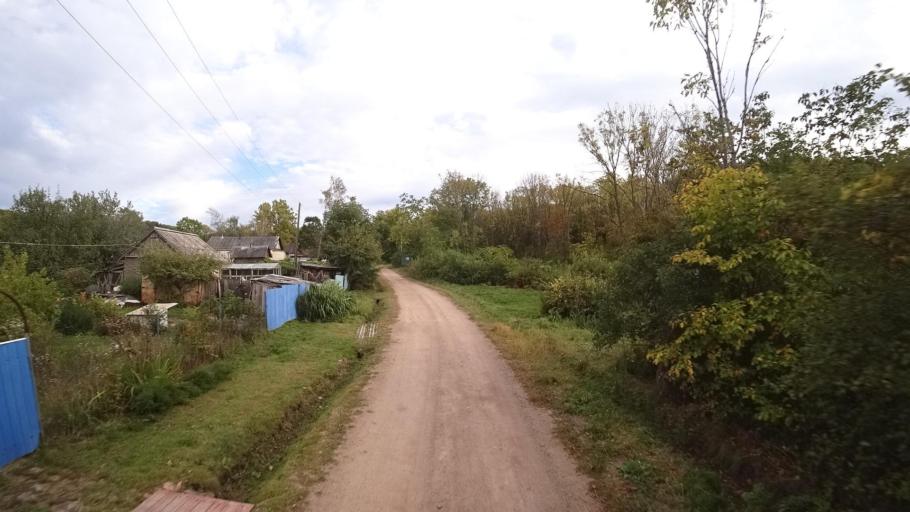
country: RU
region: Primorskiy
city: Yakovlevka
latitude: 44.4122
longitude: 133.4512
